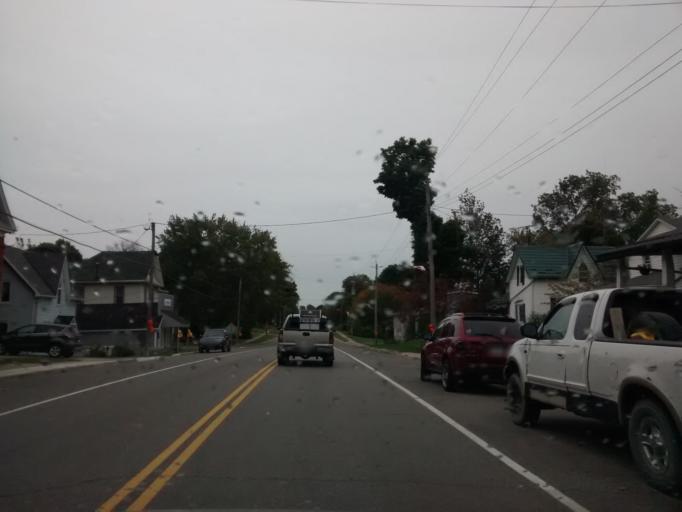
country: CA
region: Ontario
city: Ancaster
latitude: 42.8338
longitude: -79.9308
